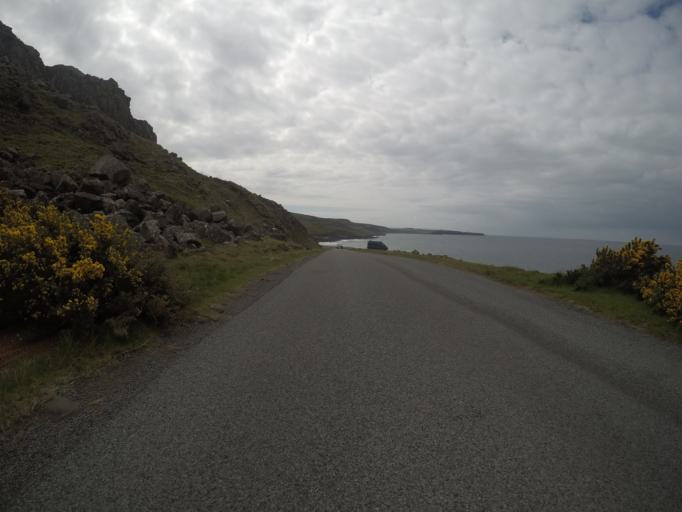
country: GB
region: Scotland
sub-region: Highland
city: Portree
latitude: 57.6741
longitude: -6.3516
